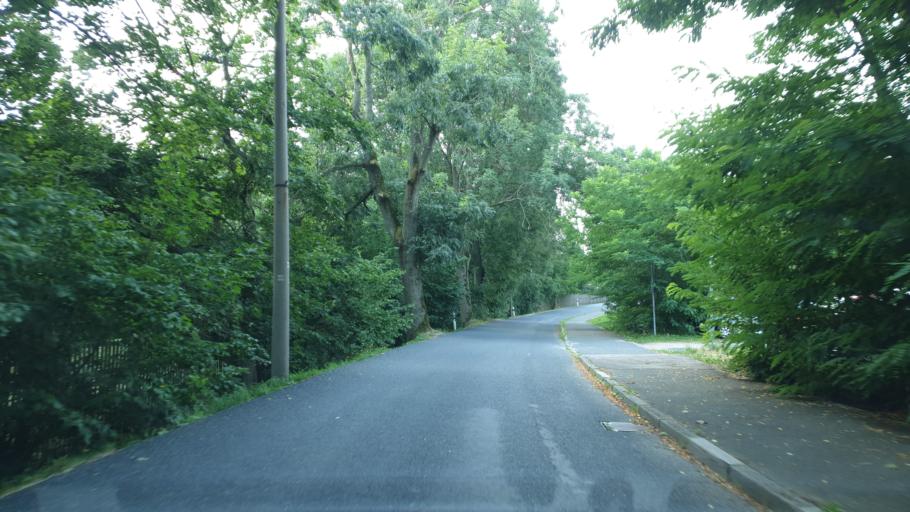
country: DE
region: Saxony
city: Hirschfeld
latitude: 50.6295
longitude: 12.4395
